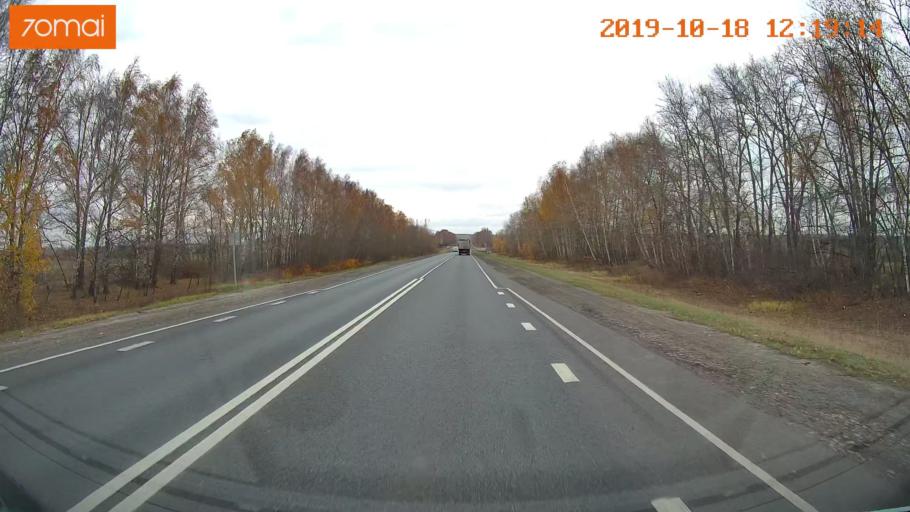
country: RU
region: Rjazan
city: Zakharovo
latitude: 54.4793
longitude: 39.4658
